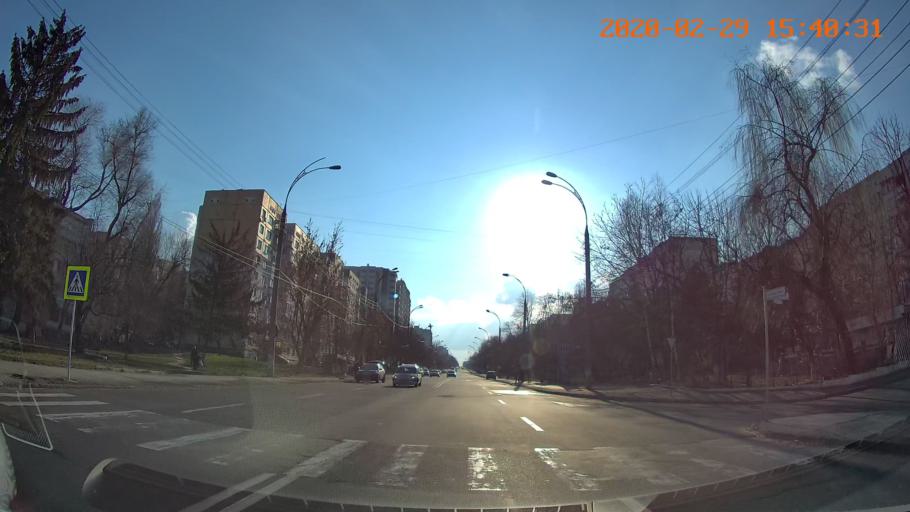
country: MD
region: Chisinau
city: Chisinau
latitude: 46.9863
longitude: 28.8671
